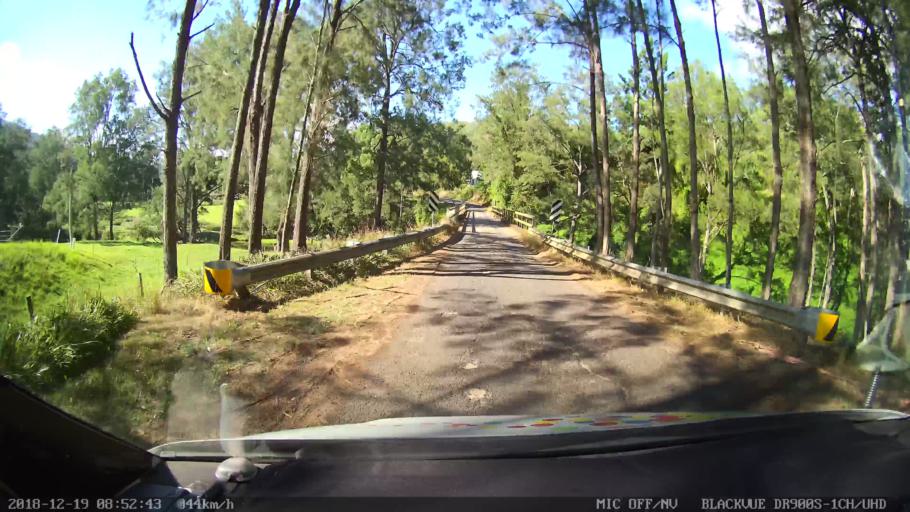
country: AU
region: New South Wales
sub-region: Kyogle
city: Kyogle
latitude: -28.3969
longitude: 152.9765
